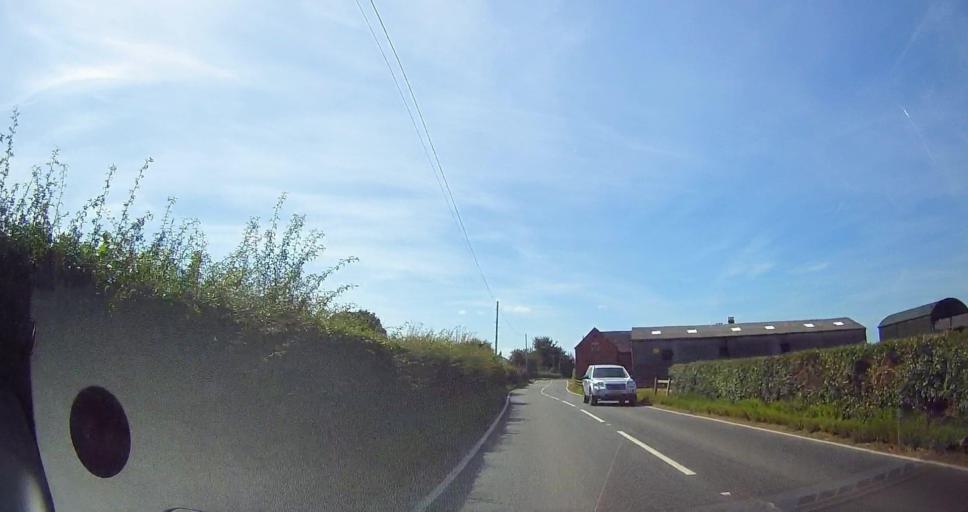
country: GB
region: England
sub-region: Cheshire East
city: Nantwich
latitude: 52.9836
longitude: -2.5249
